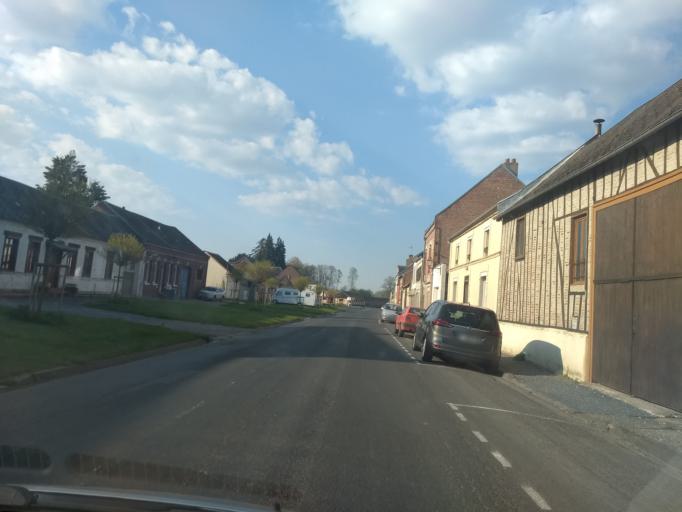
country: FR
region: Picardie
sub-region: Departement de la Somme
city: Albert
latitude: 50.0800
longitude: 2.6032
